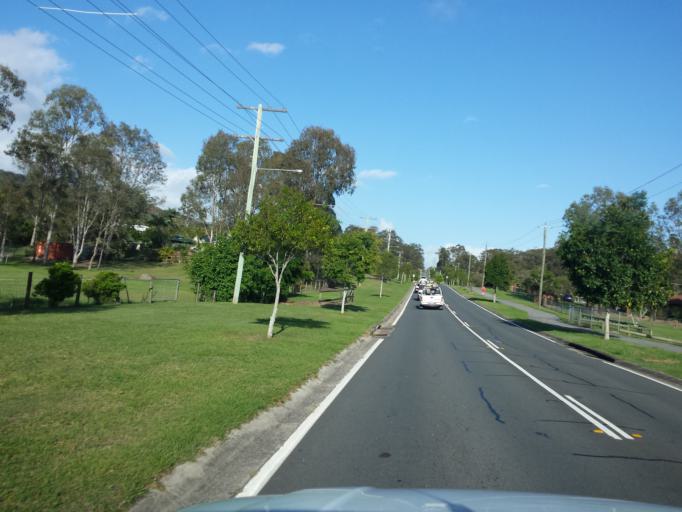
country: AU
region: Queensland
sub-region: Gold Coast
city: Ormeau Hills
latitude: -27.7807
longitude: 153.2389
